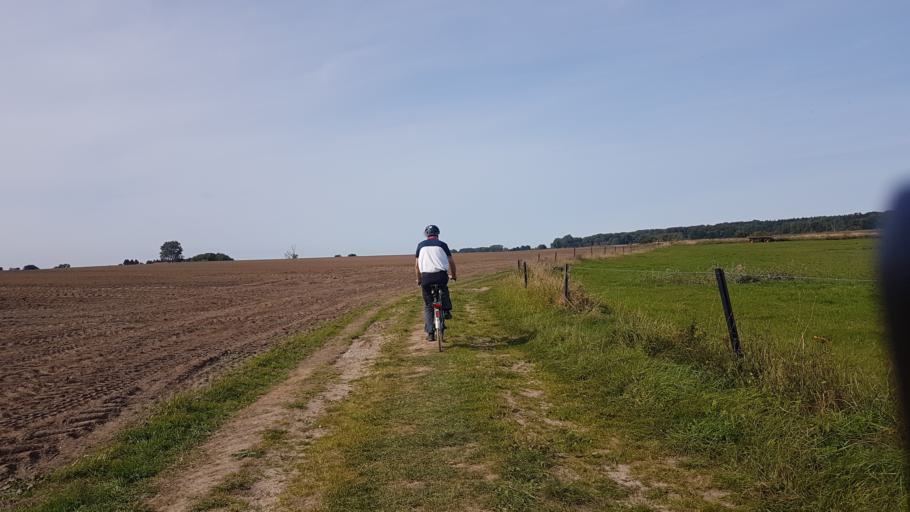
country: DE
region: Mecklenburg-Vorpommern
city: Samtens
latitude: 54.3780
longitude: 13.2668
